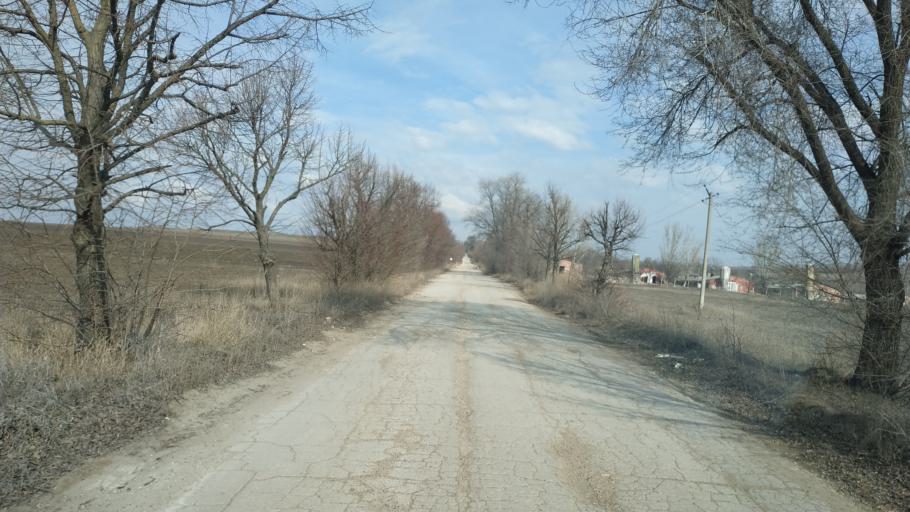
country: MD
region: Anenii Noi
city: Anenii Noi
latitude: 46.9386
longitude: 29.1088
